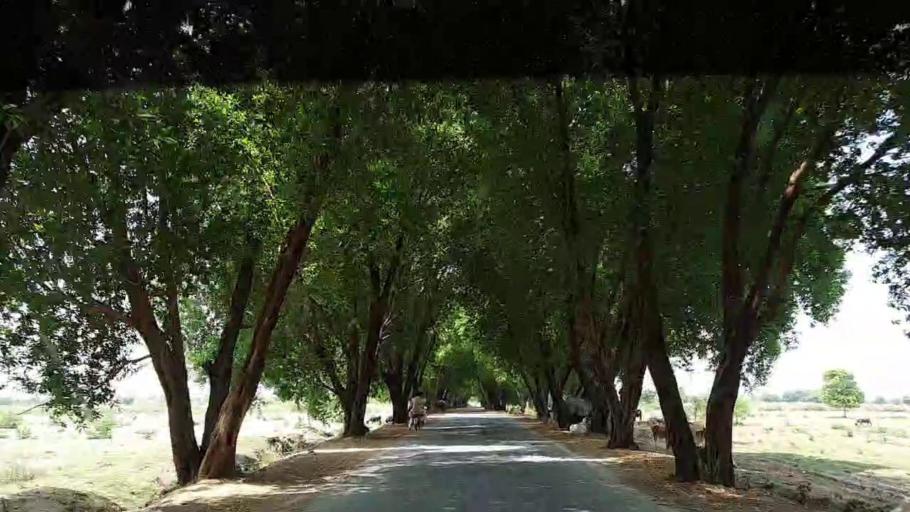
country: PK
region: Sindh
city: Adilpur
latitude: 27.8761
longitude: 69.2738
